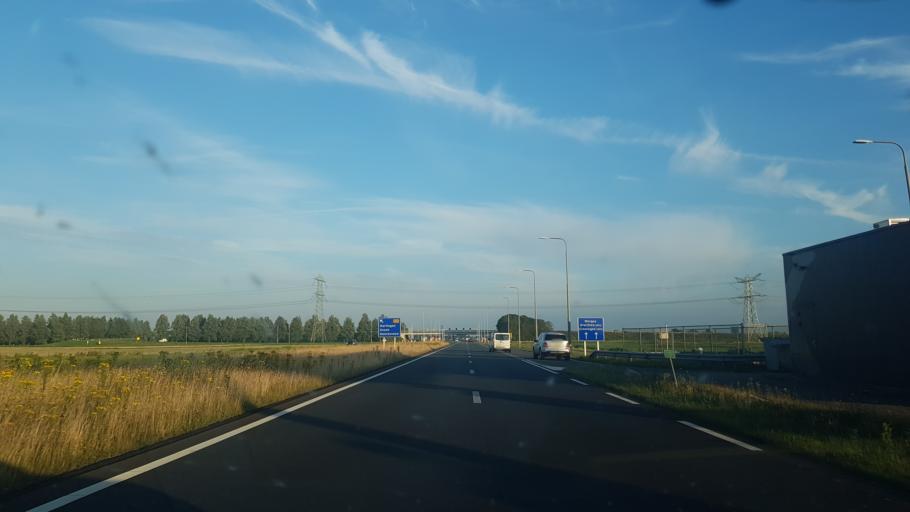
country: NL
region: Friesland
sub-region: Gemeente Leeuwarden
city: Goutum
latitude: 53.1711
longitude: 5.8270
